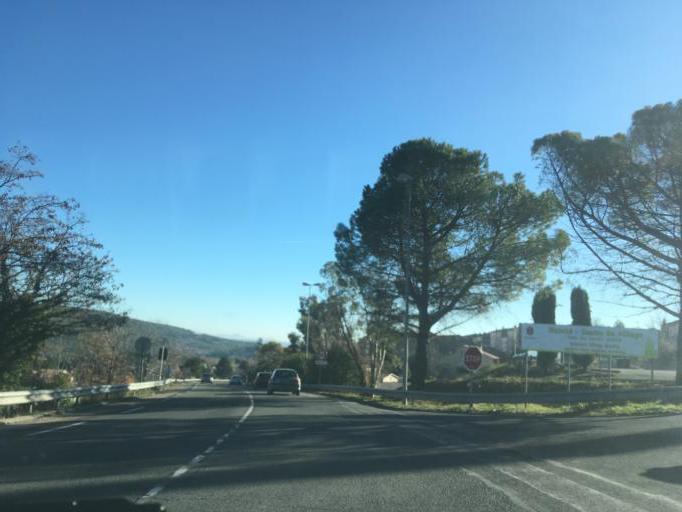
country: FR
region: Provence-Alpes-Cote d'Azur
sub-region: Departement du Var
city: Flayosc
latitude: 43.5358
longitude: 6.3913
